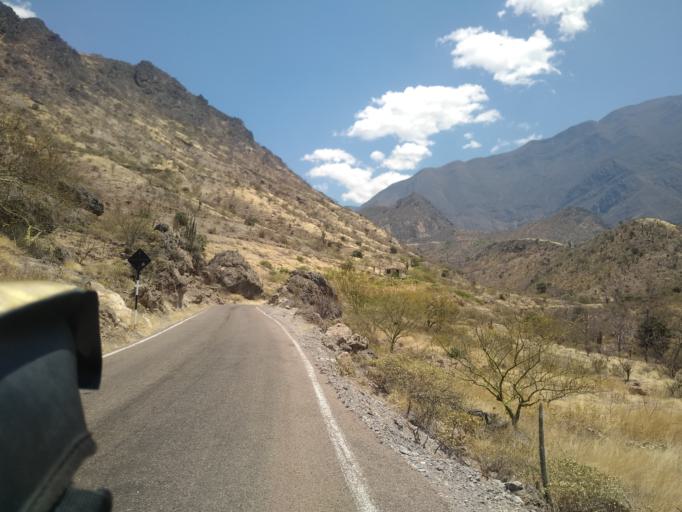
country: PE
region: Amazonas
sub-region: Provincia de Chachapoyas
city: Balsas
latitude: -6.8530
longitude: -78.0322
